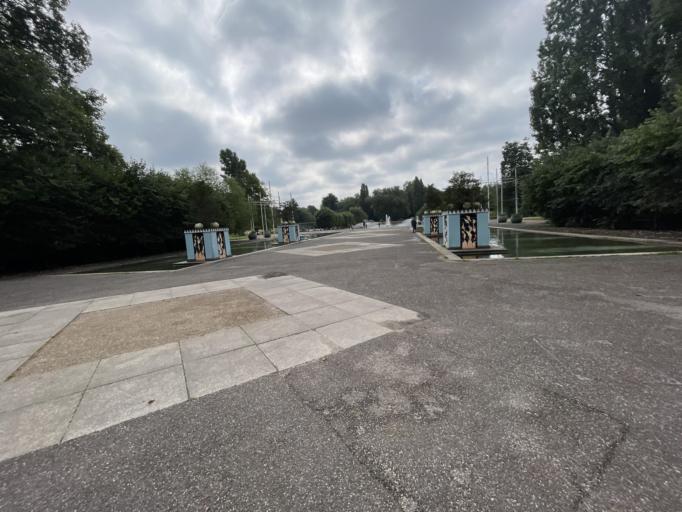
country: GB
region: England
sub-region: Greater London
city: Battersea
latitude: 51.4810
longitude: -0.1609
